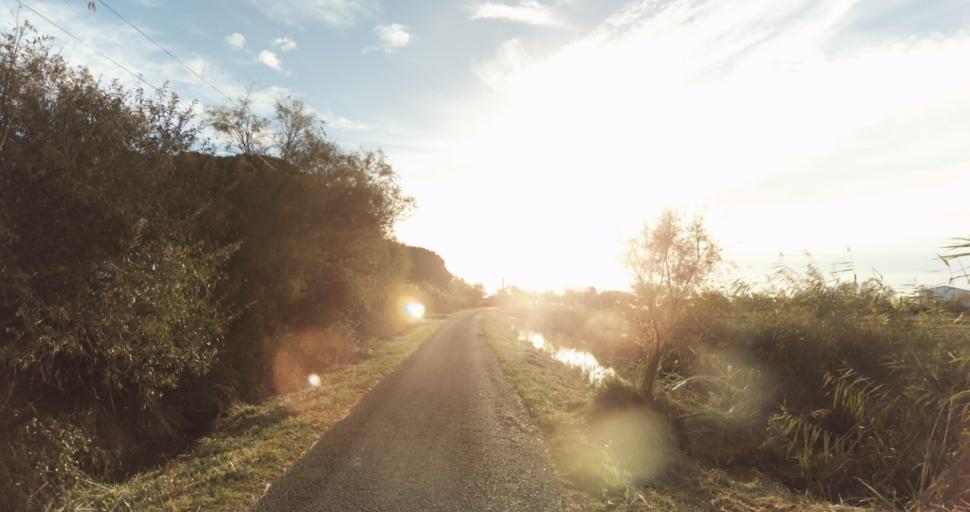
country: FR
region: Languedoc-Roussillon
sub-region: Departement du Gard
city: Aigues-Mortes
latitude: 43.5545
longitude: 4.2101
